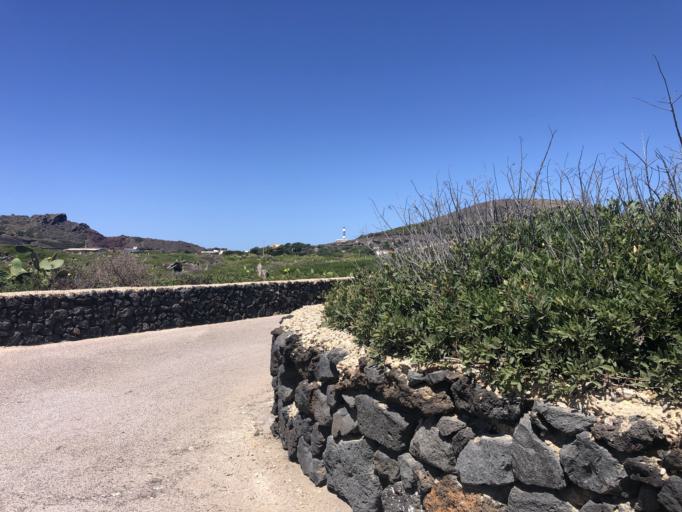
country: IT
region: Sicily
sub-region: Agrigento
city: Lampedusa
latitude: 35.8567
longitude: 12.8591
